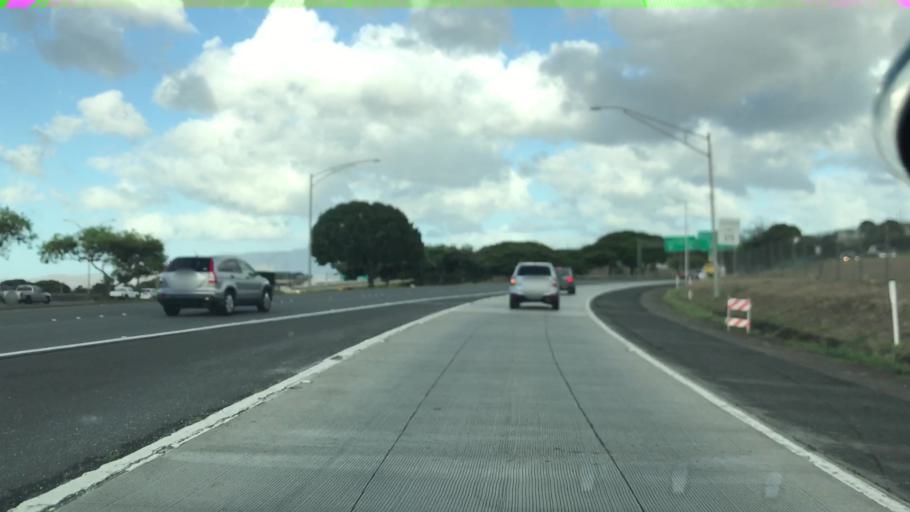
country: US
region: Hawaii
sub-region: Honolulu County
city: Halawa Heights
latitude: 21.3714
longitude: -157.9156
